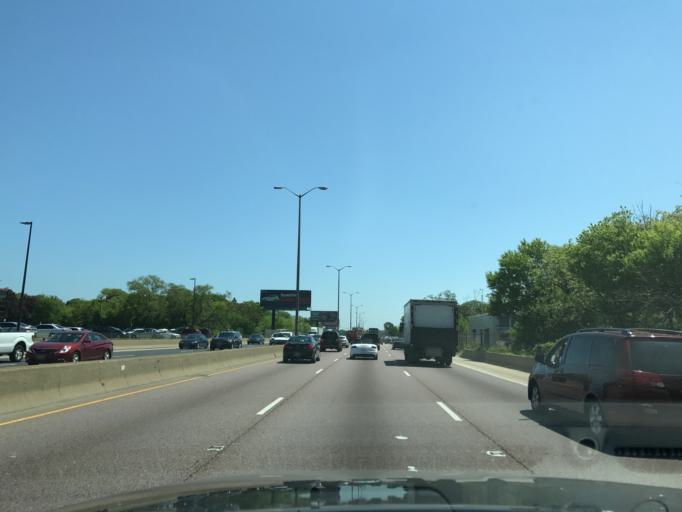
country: US
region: Illinois
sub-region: Cook County
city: Forest Park
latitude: 41.8721
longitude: -87.8274
